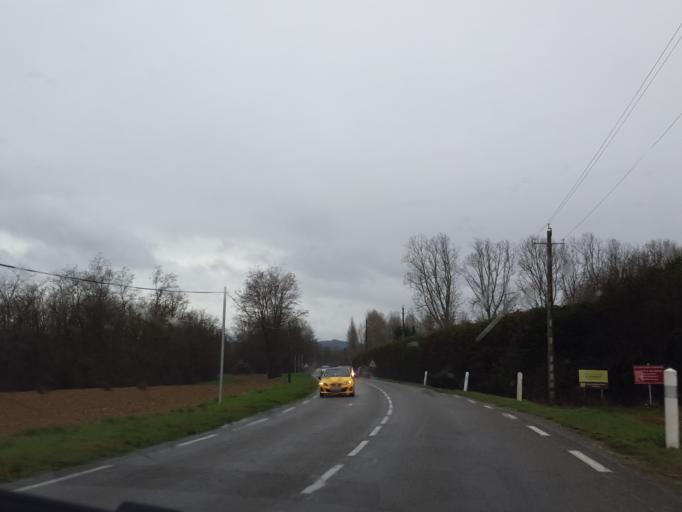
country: FR
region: Midi-Pyrenees
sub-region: Departement de l'Ariege
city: Mirepoix
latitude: 43.0990
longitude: 1.9009
